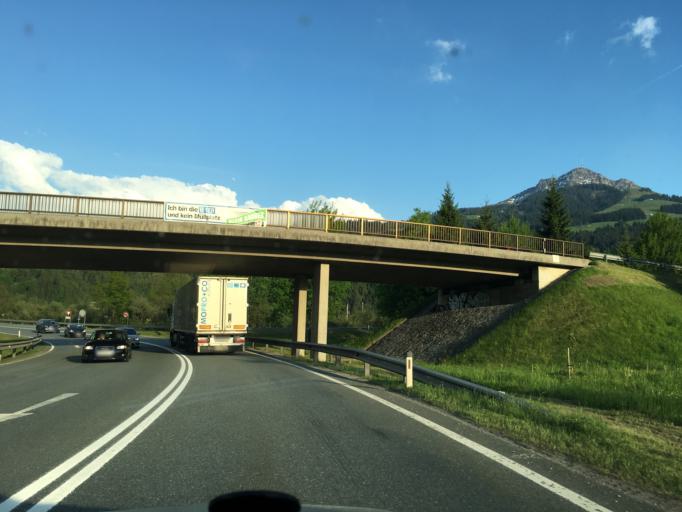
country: AT
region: Tyrol
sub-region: Politischer Bezirk Kitzbuhel
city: Sankt Johann in Tirol
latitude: 47.5172
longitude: 12.4091
